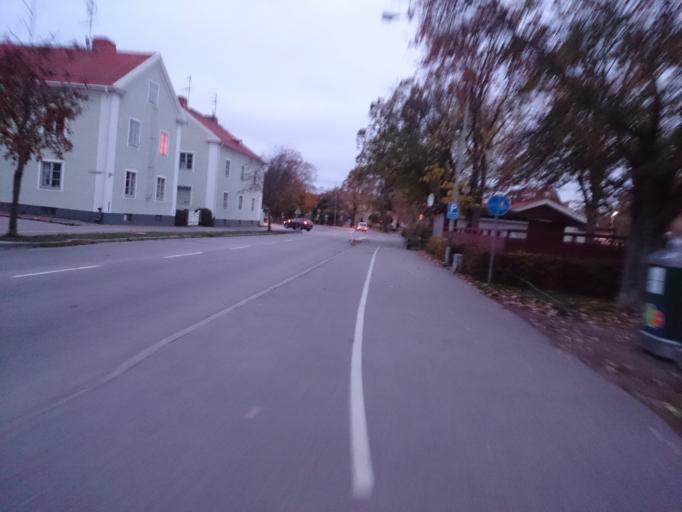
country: SE
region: Soedermanland
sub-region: Nykopings Kommun
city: Nykoping
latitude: 58.7551
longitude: 17.0213
